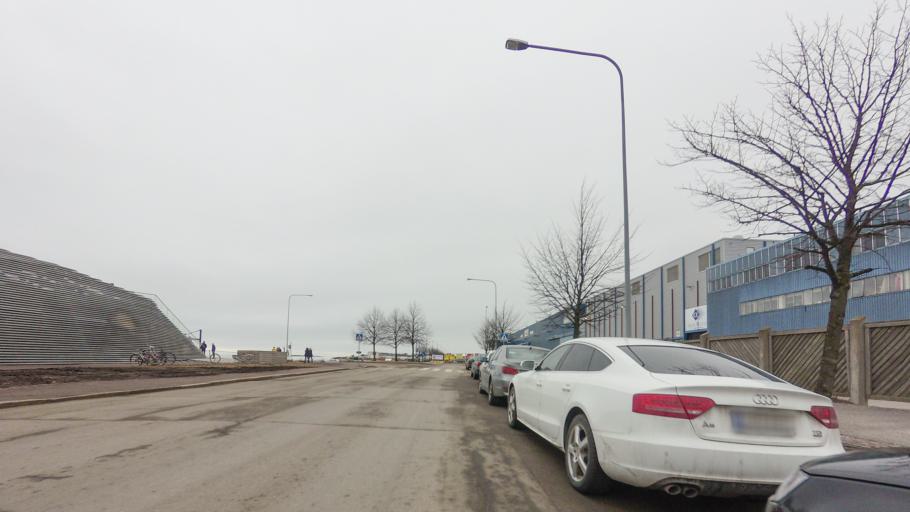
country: FI
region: Uusimaa
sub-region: Helsinki
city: Helsinki
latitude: 60.1524
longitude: 24.9300
